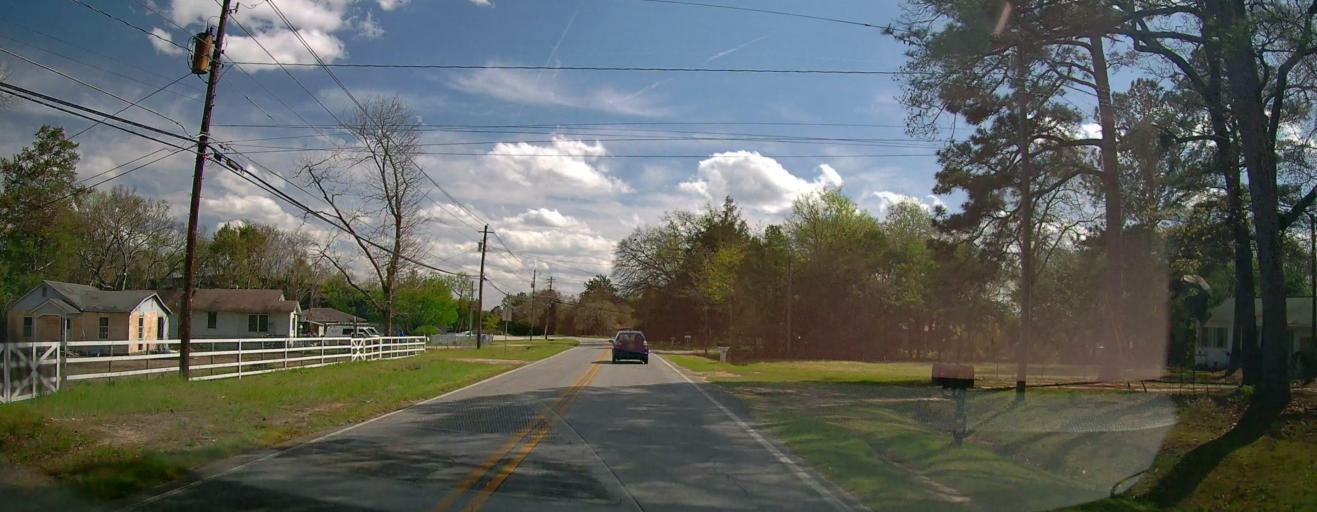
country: US
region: Georgia
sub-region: Bibb County
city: Macon
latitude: 32.8310
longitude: -83.5621
